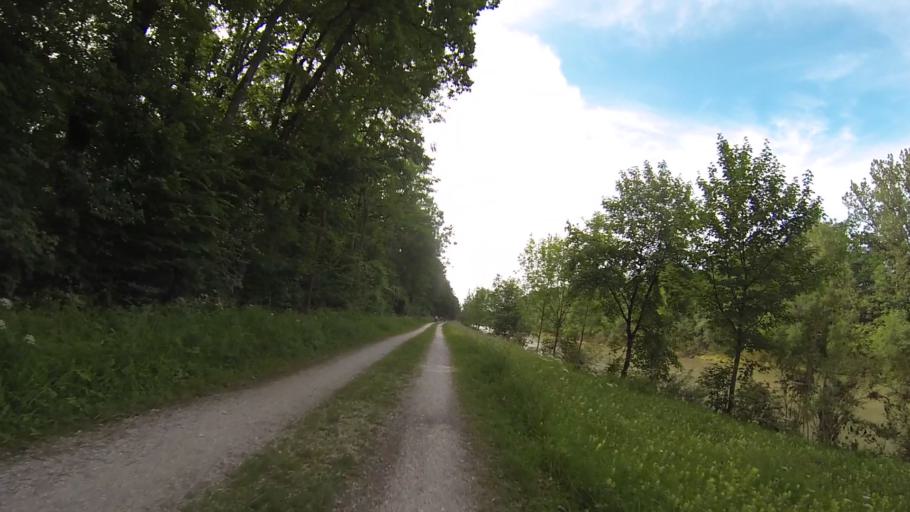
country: DE
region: Bavaria
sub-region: Swabia
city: Senden
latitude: 48.3344
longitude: 10.0138
